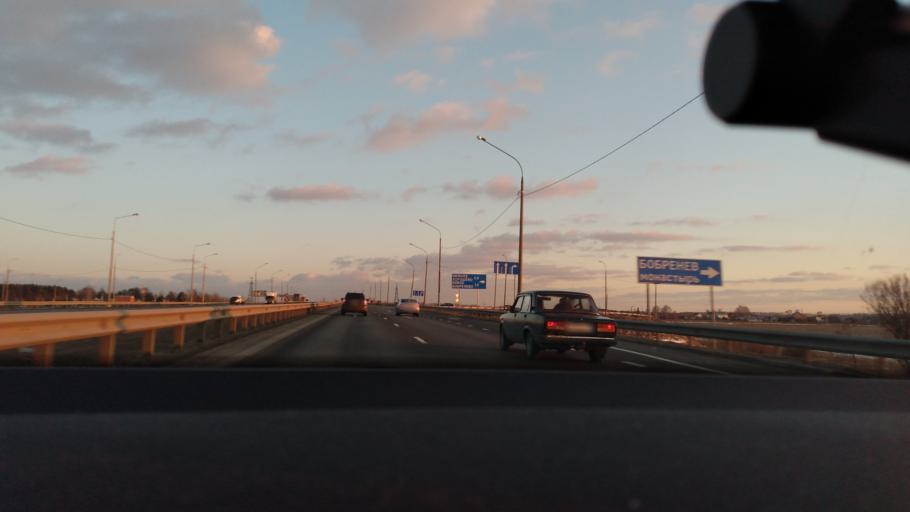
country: RU
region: Moskovskaya
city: Raduzhnyy
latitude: 55.1344
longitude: 38.7717
